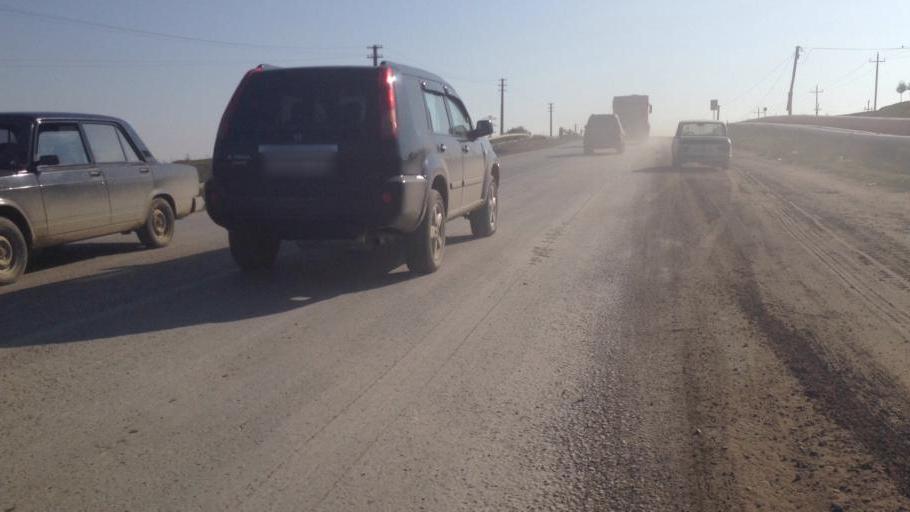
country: AZ
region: Baki
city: Balakhani
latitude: 40.4642
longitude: 49.8883
